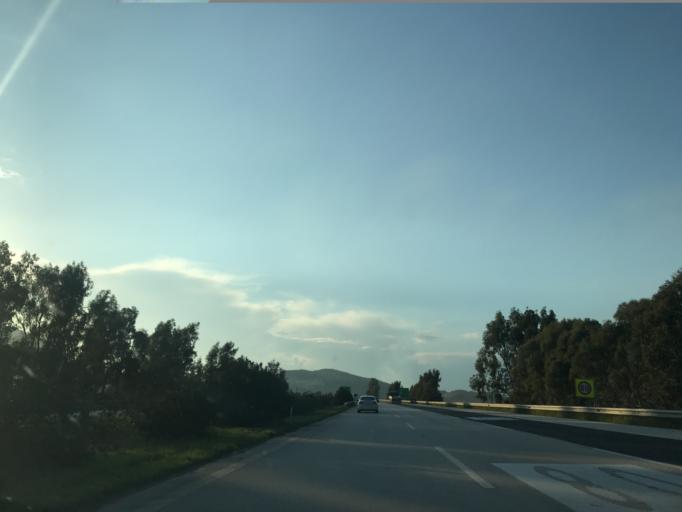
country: TR
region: Adana
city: Ceyhan
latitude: 36.9849
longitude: 35.7696
